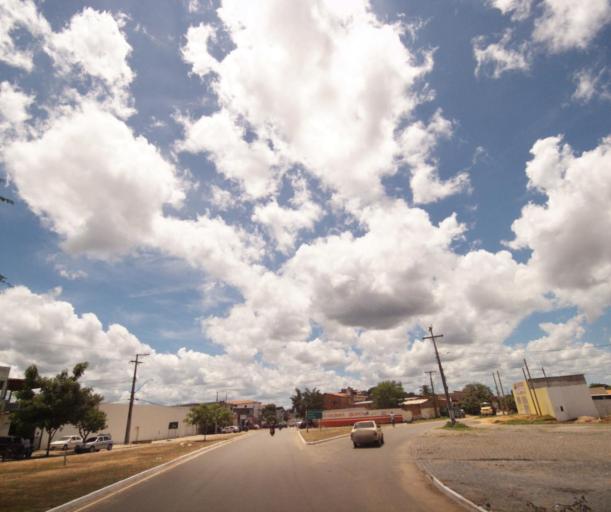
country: BR
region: Bahia
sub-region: Bom Jesus Da Lapa
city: Bom Jesus da Lapa
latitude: -13.2675
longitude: -43.4093
